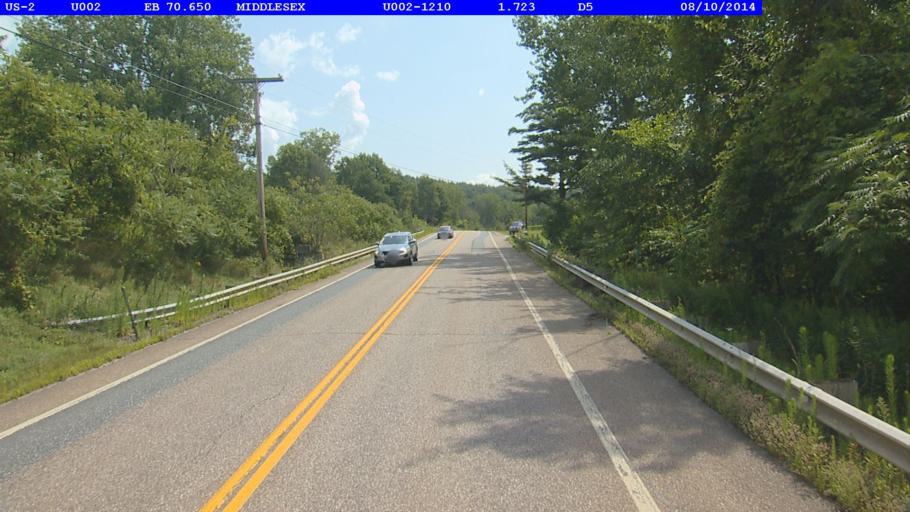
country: US
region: Vermont
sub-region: Washington County
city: Waterbury
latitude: 44.2914
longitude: -72.6715
